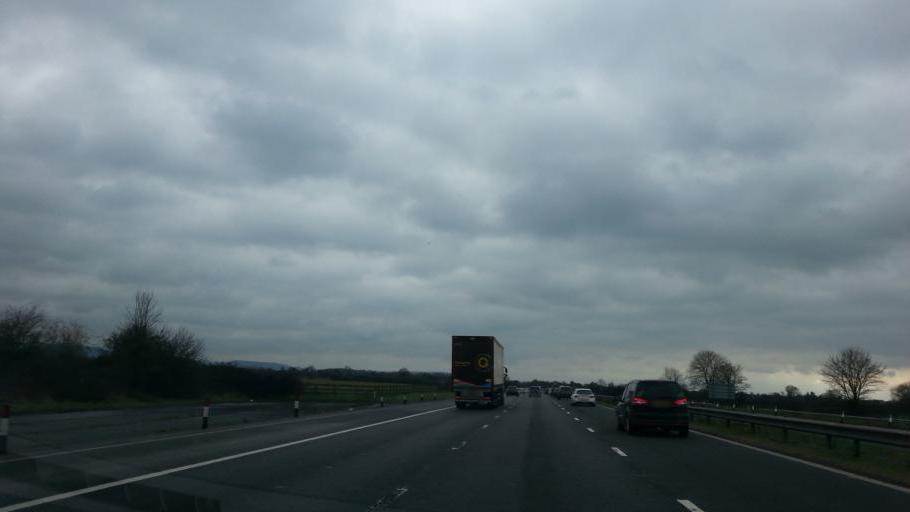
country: GB
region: England
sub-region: Gloucestershire
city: Stonehouse
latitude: 51.7871
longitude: -2.3004
